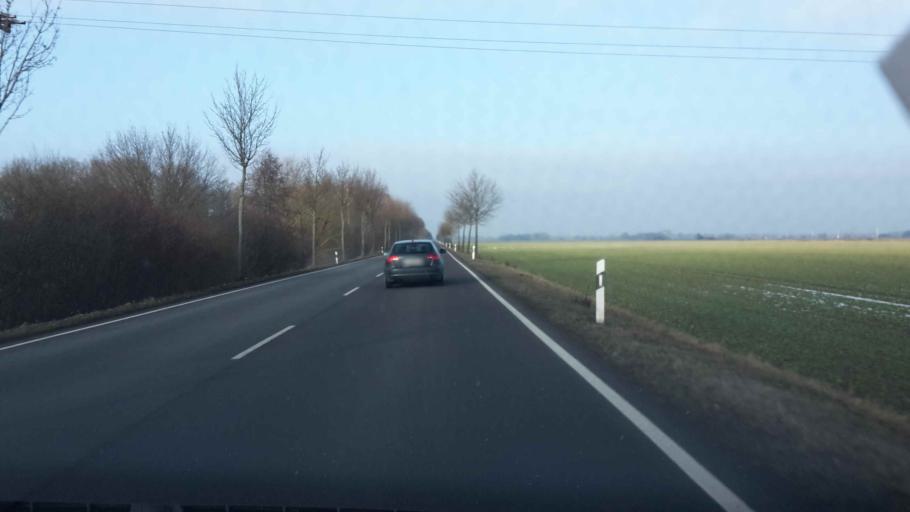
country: DE
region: Saxony-Anhalt
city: Seehausen
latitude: 52.9163
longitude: 11.7339
